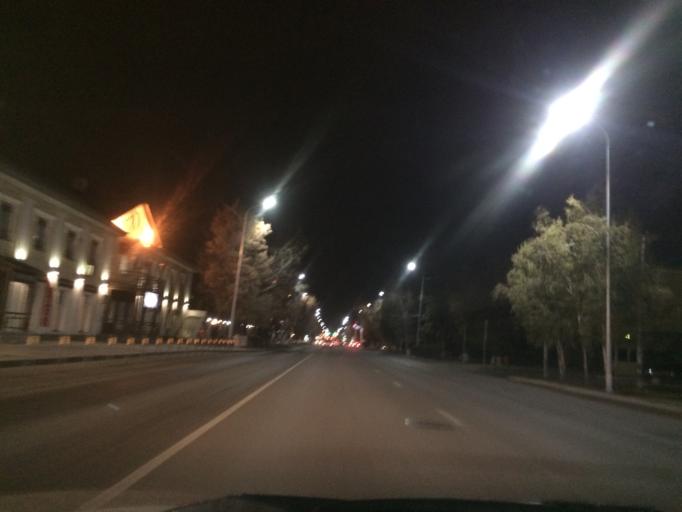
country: KZ
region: Astana Qalasy
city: Astana
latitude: 51.1645
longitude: 71.4202
